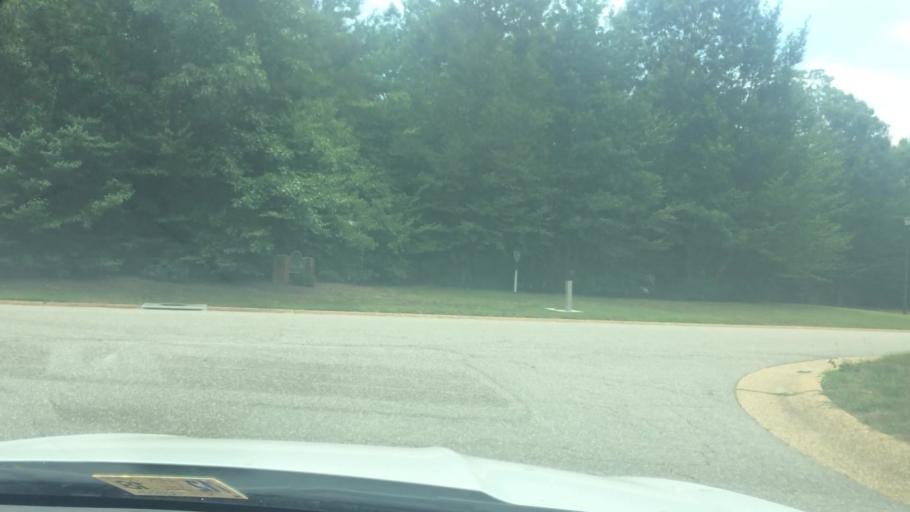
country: US
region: Virginia
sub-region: James City County
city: Williamsburg
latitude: 37.2725
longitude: -76.8178
